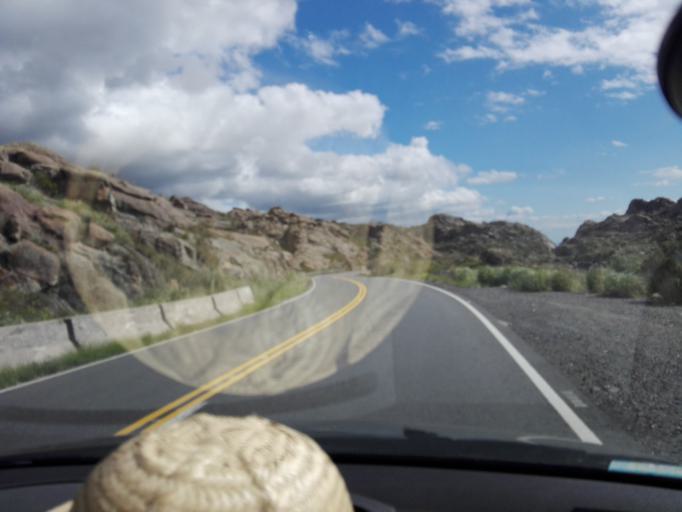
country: AR
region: Cordoba
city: Mina Clavero
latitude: -31.7586
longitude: -64.9130
